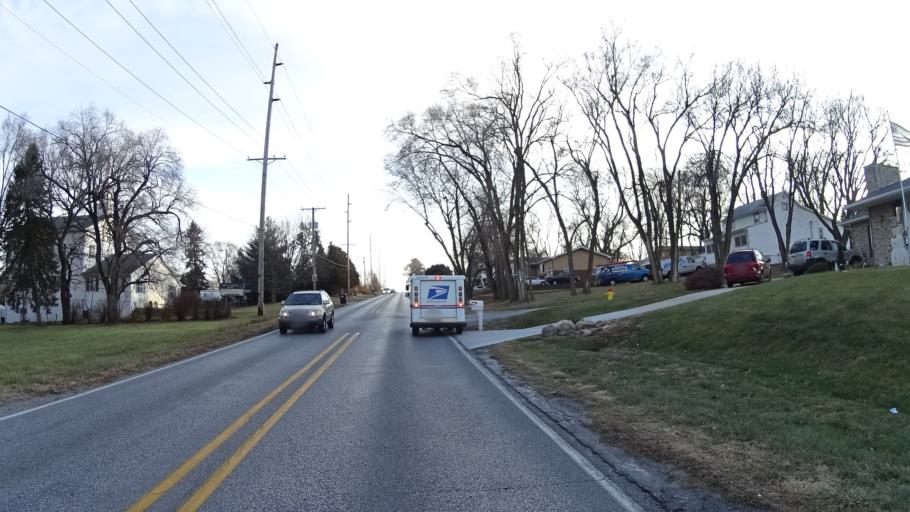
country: US
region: Nebraska
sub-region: Sarpy County
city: La Vista
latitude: 41.1741
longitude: -95.9673
